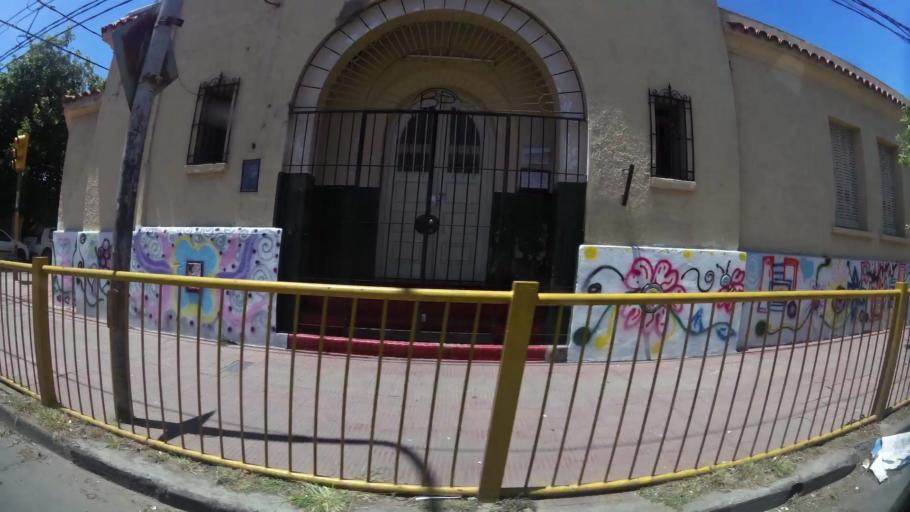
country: AR
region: Cordoba
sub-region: Departamento de Capital
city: Cordoba
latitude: -31.3952
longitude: -64.2136
